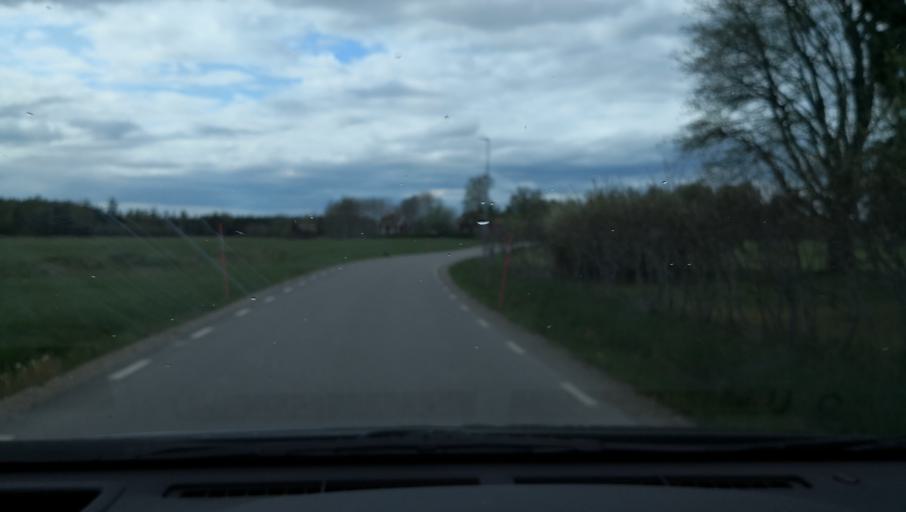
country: SE
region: Dalarna
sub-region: Avesta Kommun
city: Avesta
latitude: 60.0228
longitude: 16.2676
